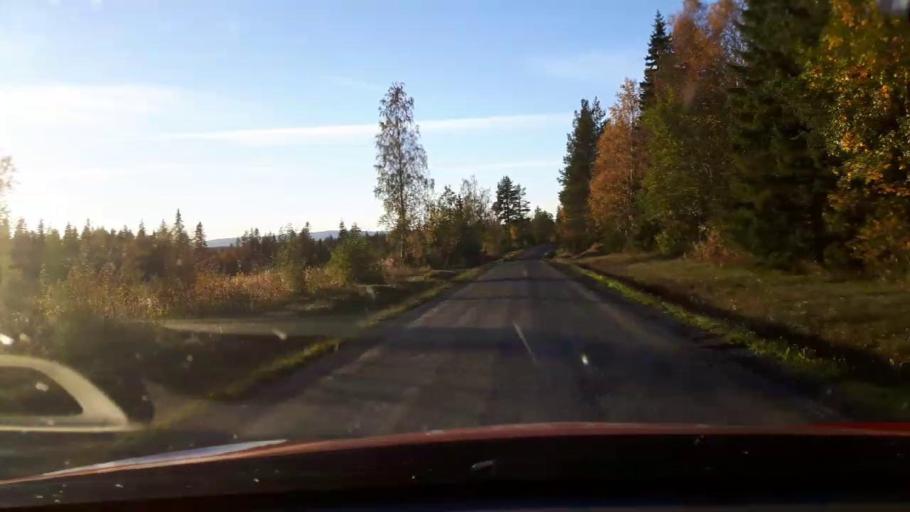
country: SE
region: Jaemtland
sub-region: Krokoms Kommun
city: Krokom
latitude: 63.4172
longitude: 14.6112
